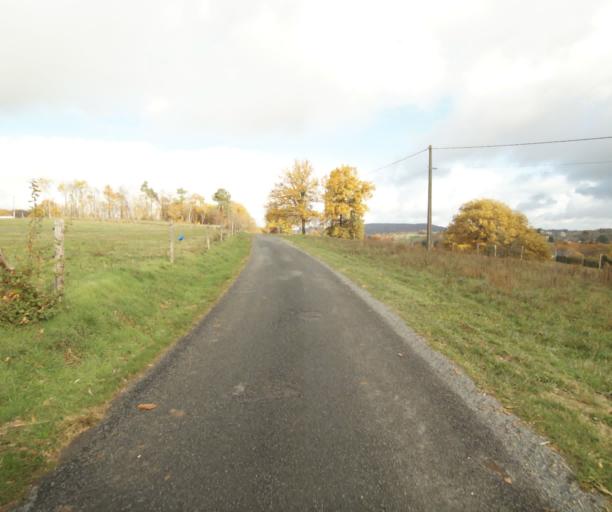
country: FR
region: Limousin
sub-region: Departement de la Correze
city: Sainte-Fereole
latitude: 45.2098
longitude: 1.6218
